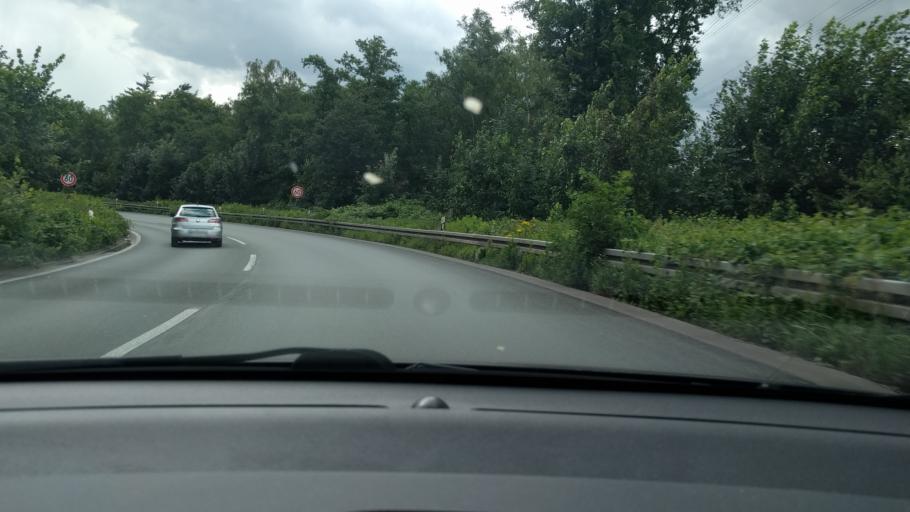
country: DE
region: North Rhine-Westphalia
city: Waltrop
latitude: 51.5872
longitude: 7.3692
